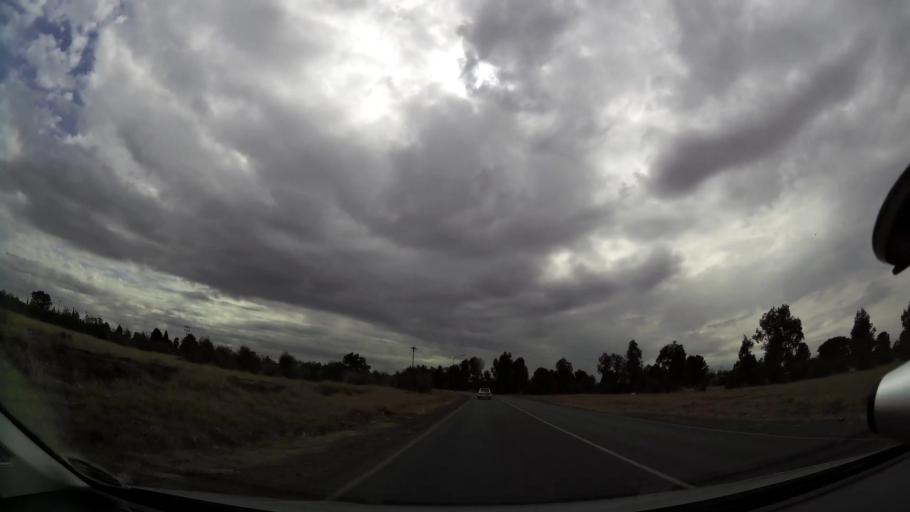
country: ZA
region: Orange Free State
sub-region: Fezile Dabi District Municipality
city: Kroonstad
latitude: -27.6453
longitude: 27.2221
